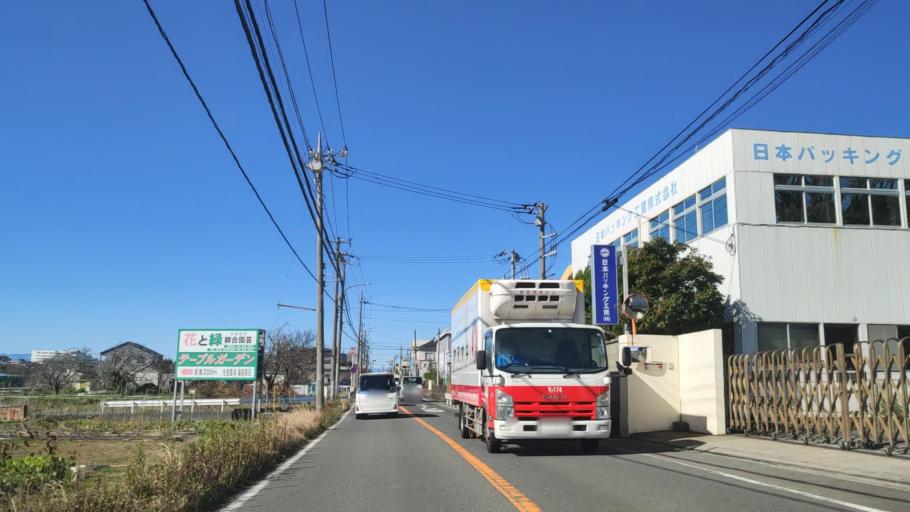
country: JP
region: Tokyo
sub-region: Machida-shi
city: Machida
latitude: 35.5269
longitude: 139.5283
